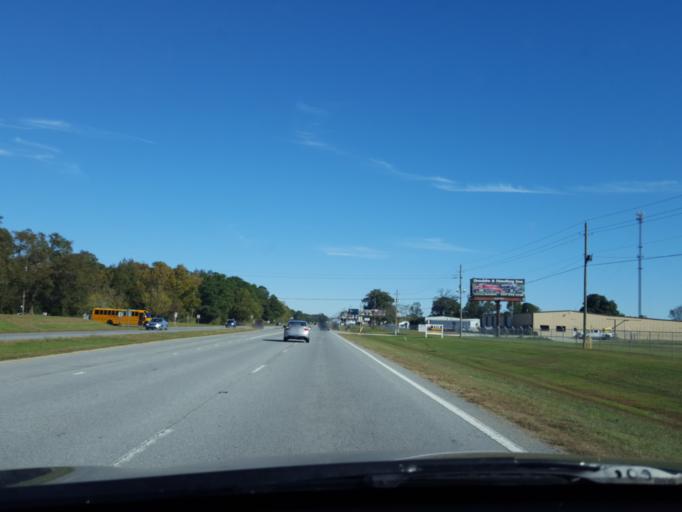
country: US
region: North Carolina
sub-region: Beaufort County
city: Washington
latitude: 35.6040
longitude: -77.1359
